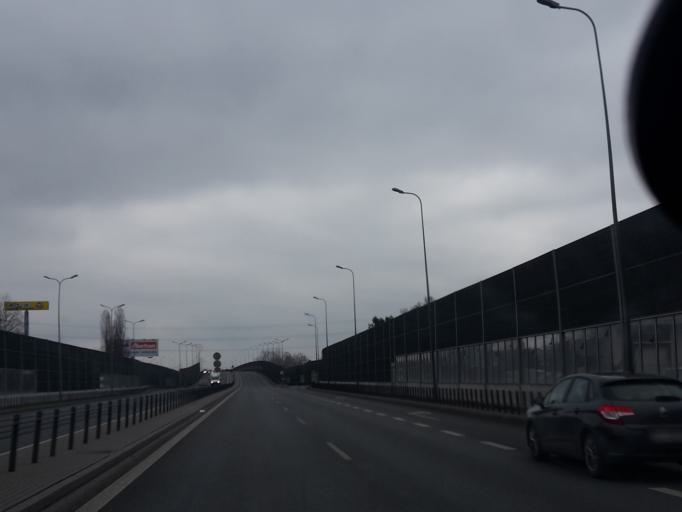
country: PL
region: Masovian Voivodeship
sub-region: Powiat warszawski zachodni
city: Lomianki
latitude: 52.3302
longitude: 20.8962
